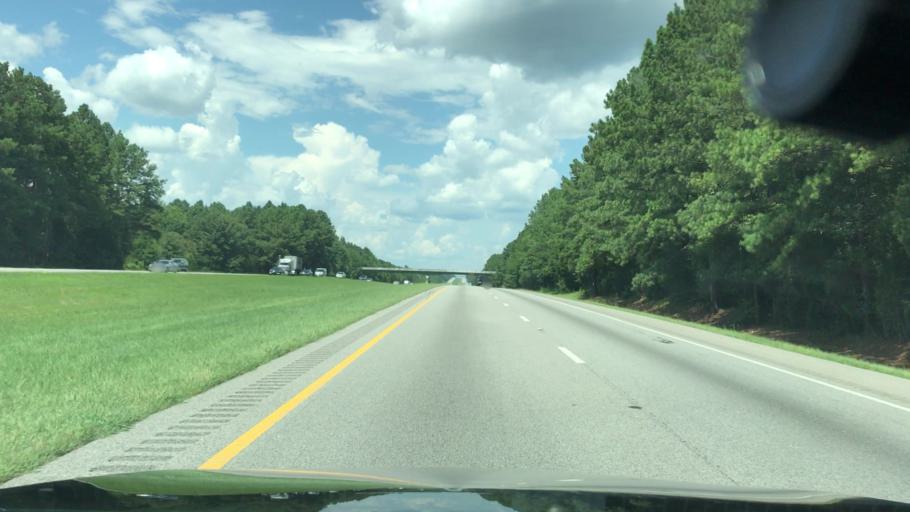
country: US
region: South Carolina
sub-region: Chester County
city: Great Falls
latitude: 34.6501
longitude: -81.0286
